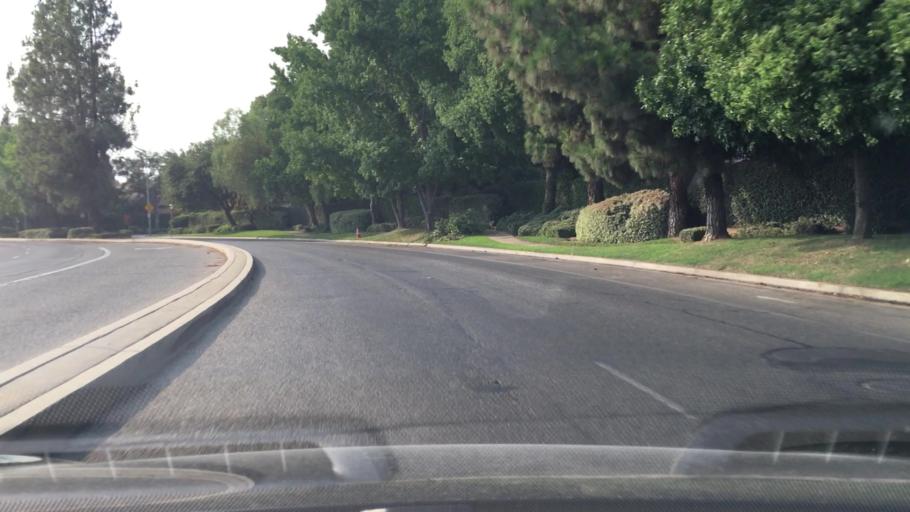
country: US
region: California
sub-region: Fresno County
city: Clovis
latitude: 36.8395
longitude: -119.7363
